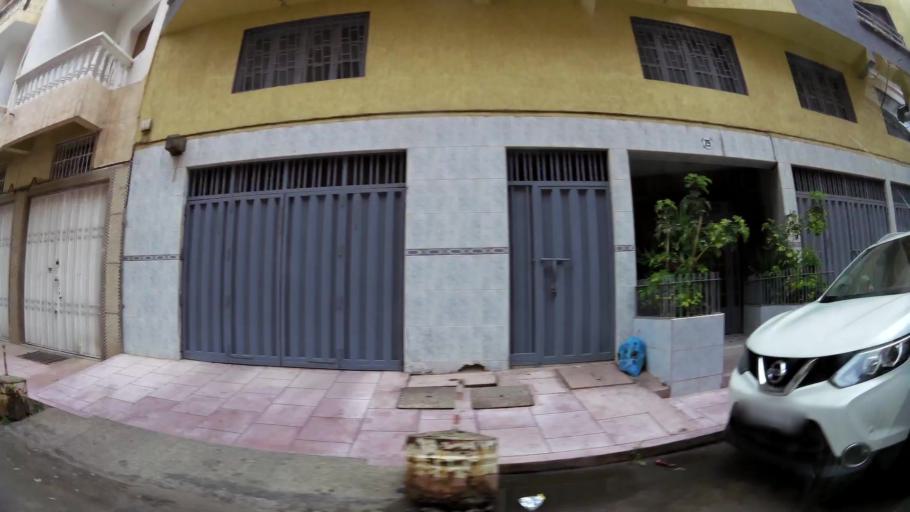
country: MA
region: Grand Casablanca
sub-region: Casablanca
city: Casablanca
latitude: 33.5326
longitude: -7.6077
